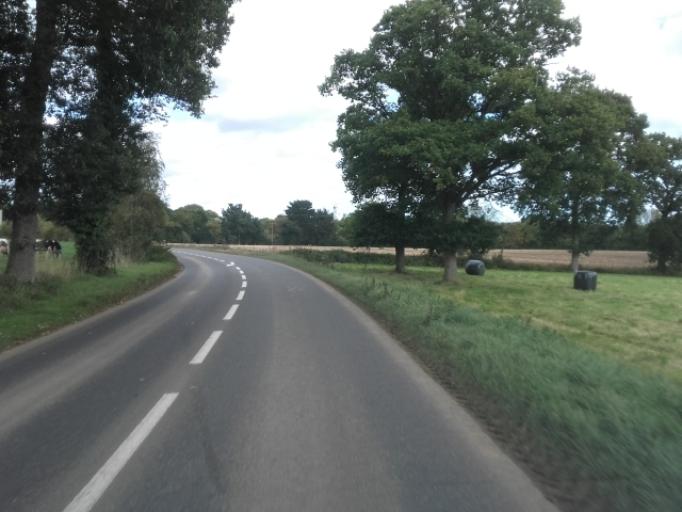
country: FR
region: Brittany
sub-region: Departement des Cotes-d'Armor
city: Lanvollon
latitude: 48.6460
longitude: -2.9655
